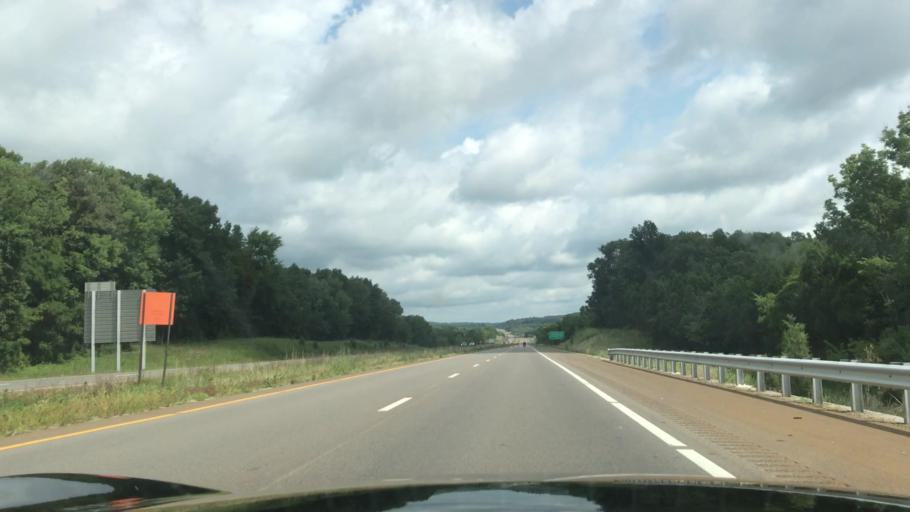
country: US
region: Kentucky
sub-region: Warren County
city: Bowling Green
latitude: 36.9711
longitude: -86.4995
